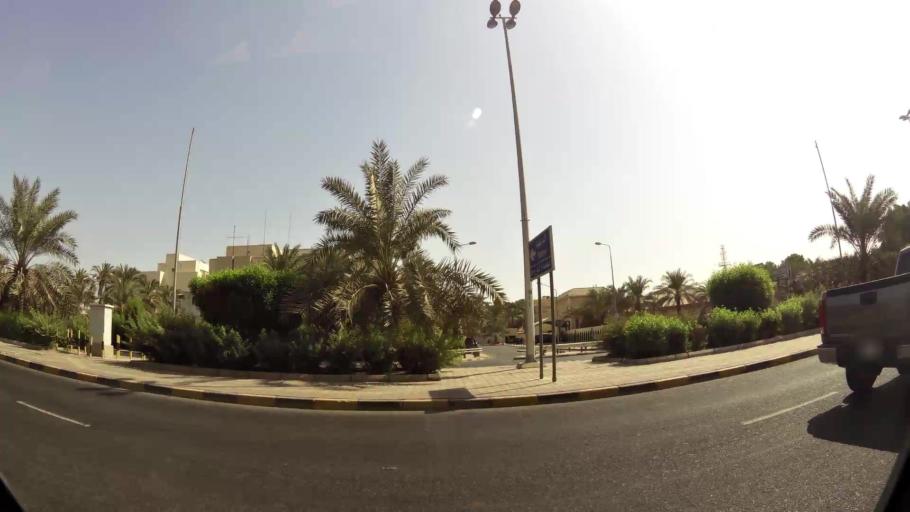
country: KW
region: Al Asimah
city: Ad Dasmah
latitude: 29.3672
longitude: 48.0117
